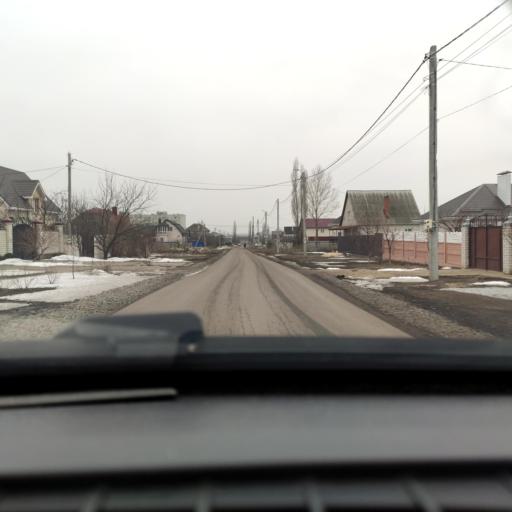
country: RU
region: Voronezj
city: Novaya Usman'
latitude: 51.6576
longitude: 39.4118
